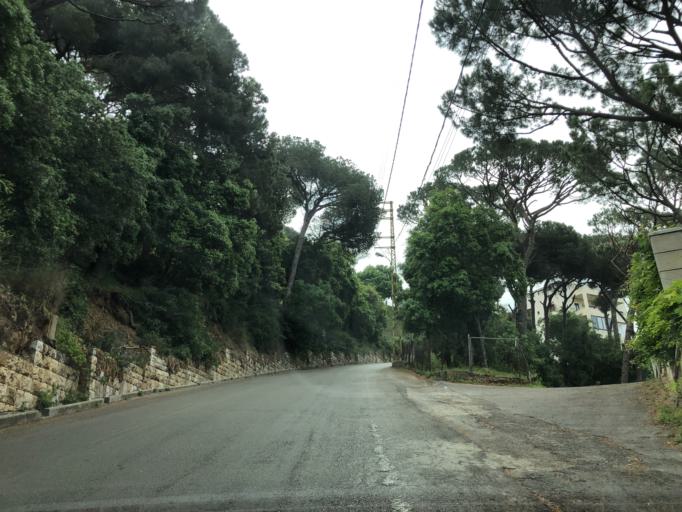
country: LB
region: Mont-Liban
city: Jdaidet el Matn
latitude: 33.8592
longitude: 35.5999
